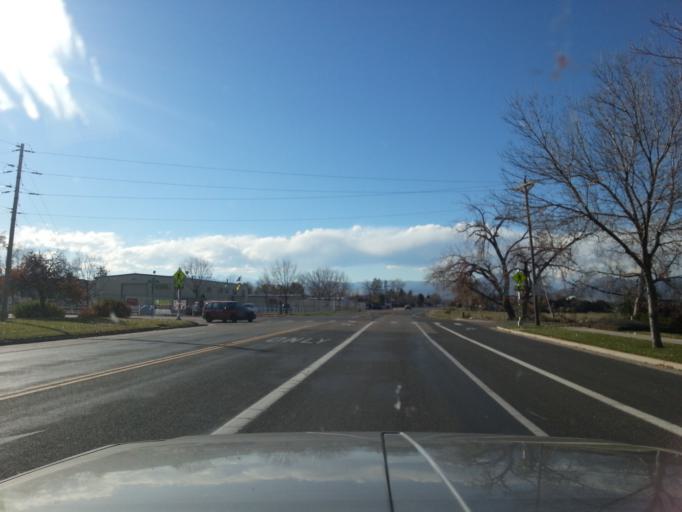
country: US
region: Colorado
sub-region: Larimer County
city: Loveland
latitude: 40.3924
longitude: -105.1058
